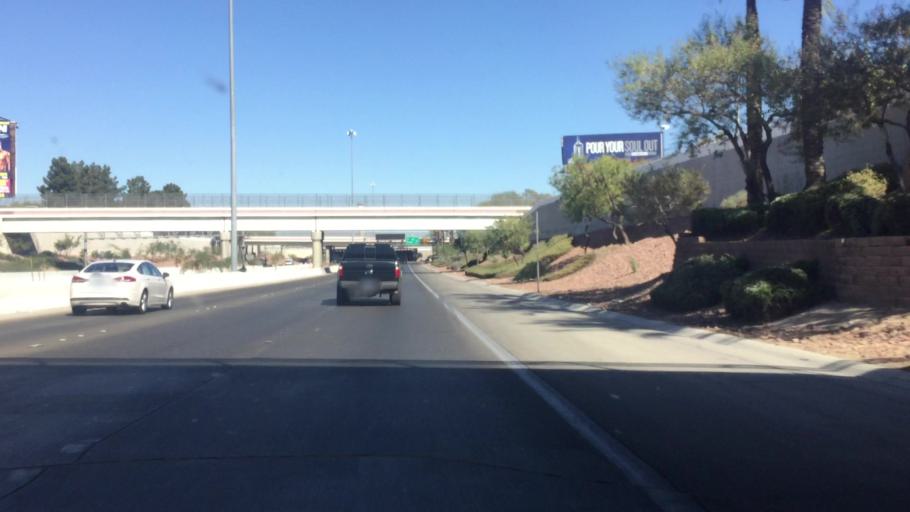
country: US
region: Nevada
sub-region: Clark County
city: Paradise
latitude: 36.0674
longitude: -115.1476
